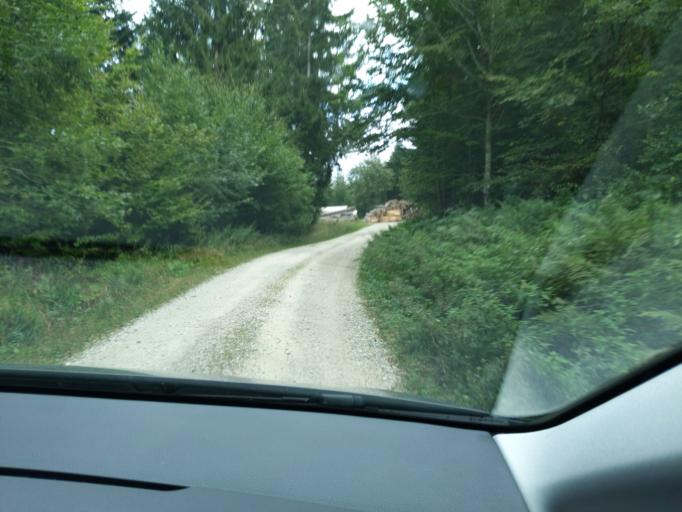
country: CH
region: Bern
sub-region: Oberaargau
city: Wyssachen
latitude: 47.0300
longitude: 7.8311
